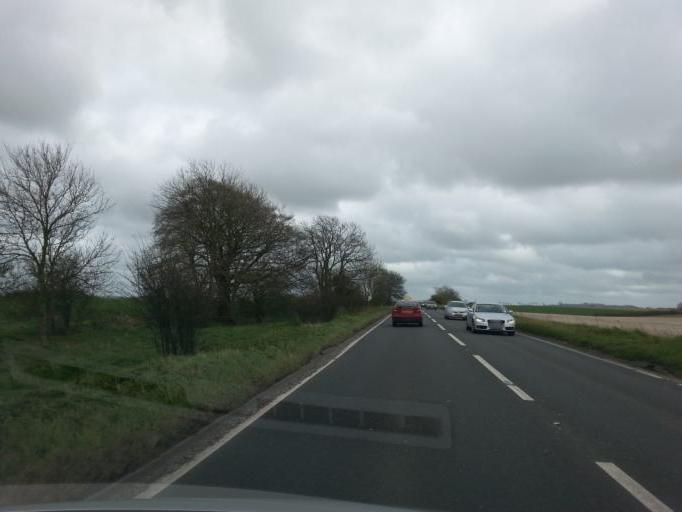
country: GB
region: England
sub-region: Wiltshire
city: Mere
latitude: 51.1031
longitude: -2.2061
